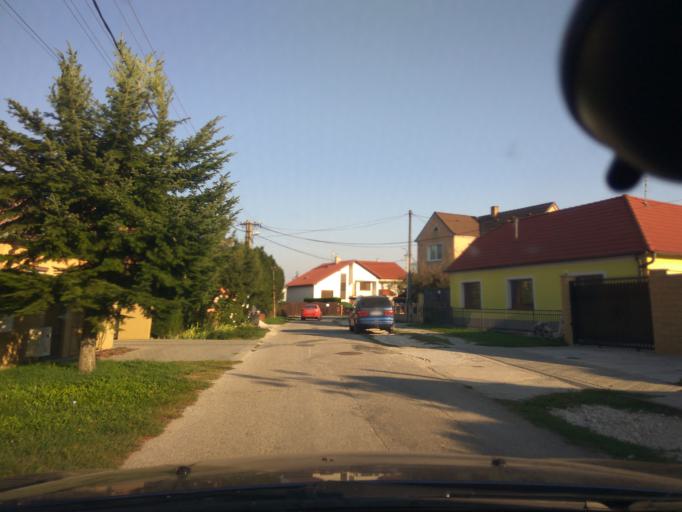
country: SK
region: Trnavsky
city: Vrbove
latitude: 48.5833
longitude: 17.7631
